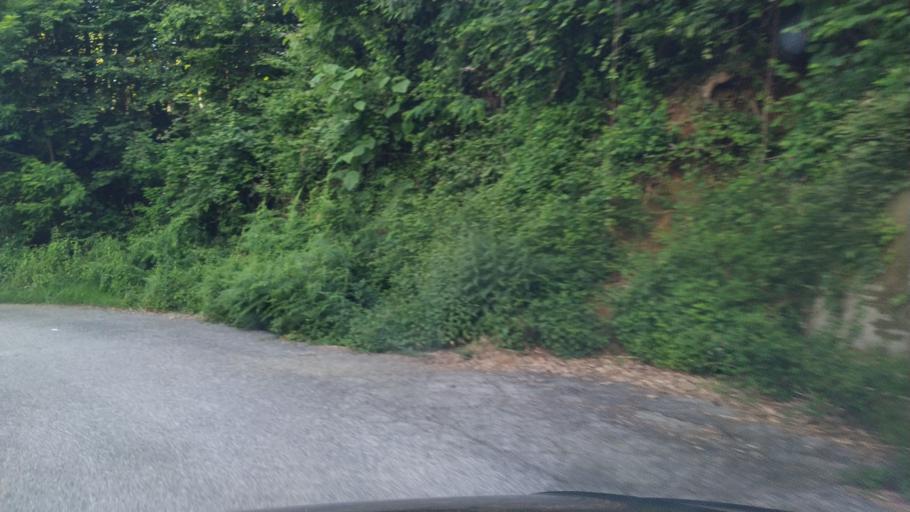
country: IT
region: Piedmont
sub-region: Provincia di Torino
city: Cintano
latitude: 45.4154
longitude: 7.7135
